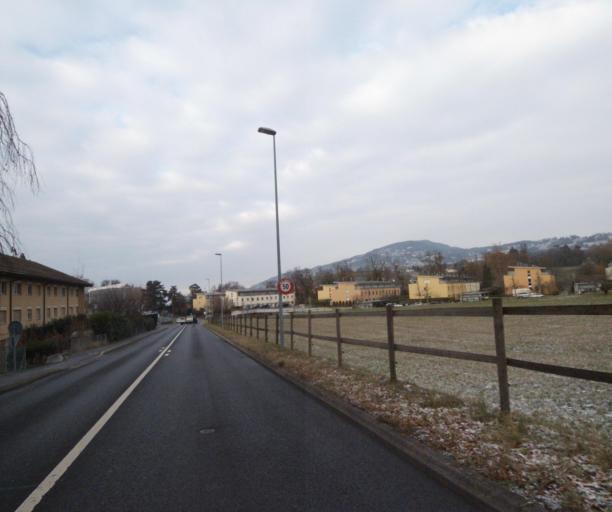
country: CH
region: Vaud
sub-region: Riviera-Pays-d'Enhaut District
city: La Tour-de-Peilz
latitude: 46.4613
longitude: 6.8704
